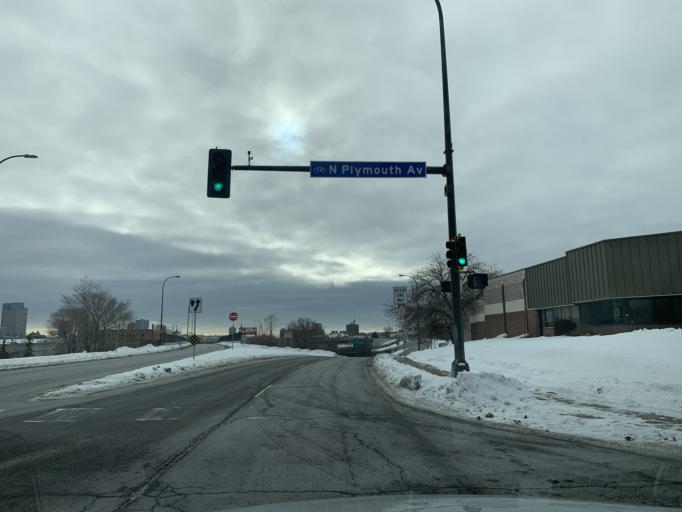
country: US
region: Minnesota
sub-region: Hennepin County
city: Minneapolis
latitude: 44.9919
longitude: -93.2881
